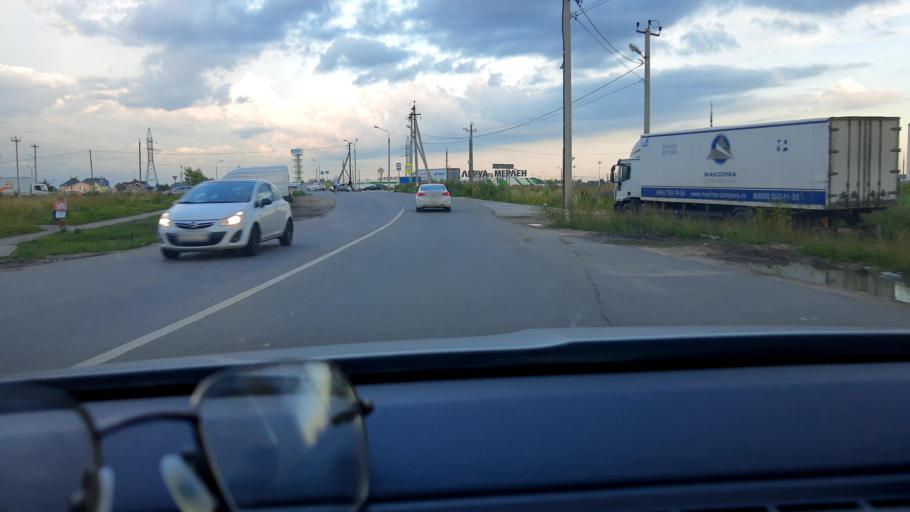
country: RU
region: Moskovskaya
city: Vostryakovo
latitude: 55.3971
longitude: 37.7737
